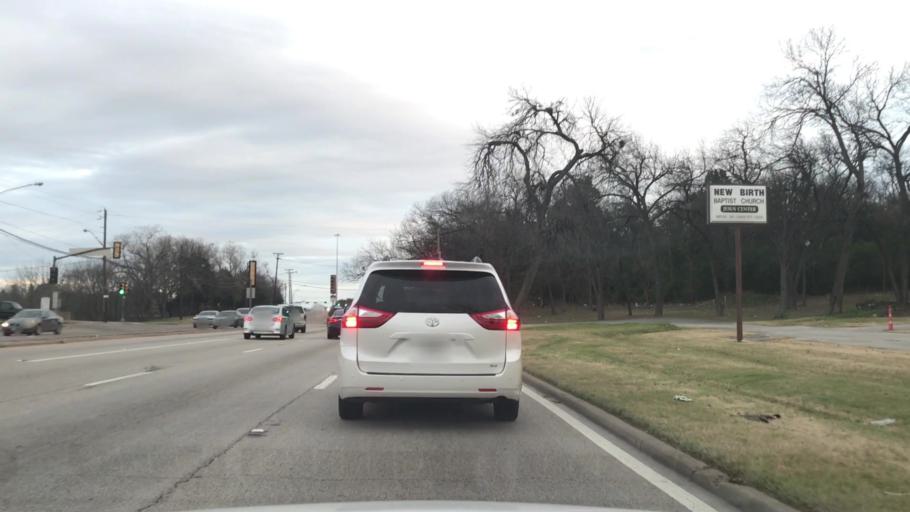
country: US
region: Texas
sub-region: Dallas County
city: Cockrell Hill
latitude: 32.6891
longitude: -96.8294
